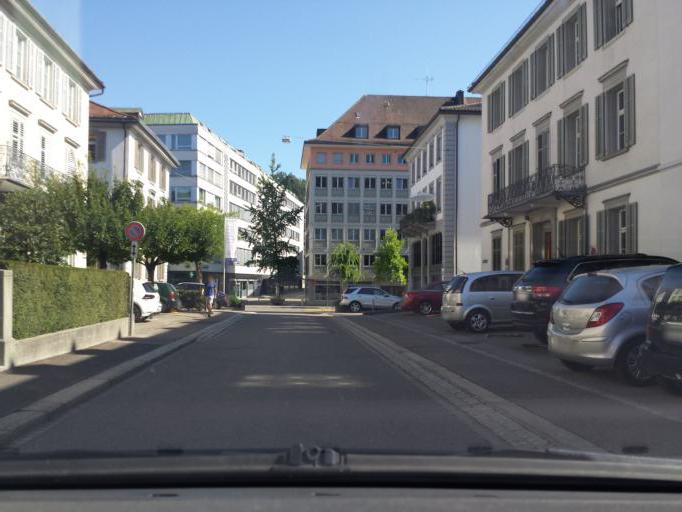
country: CH
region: Saint Gallen
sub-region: Wahlkreis St. Gallen
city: Sankt Gallen
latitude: 47.4253
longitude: 9.3729
